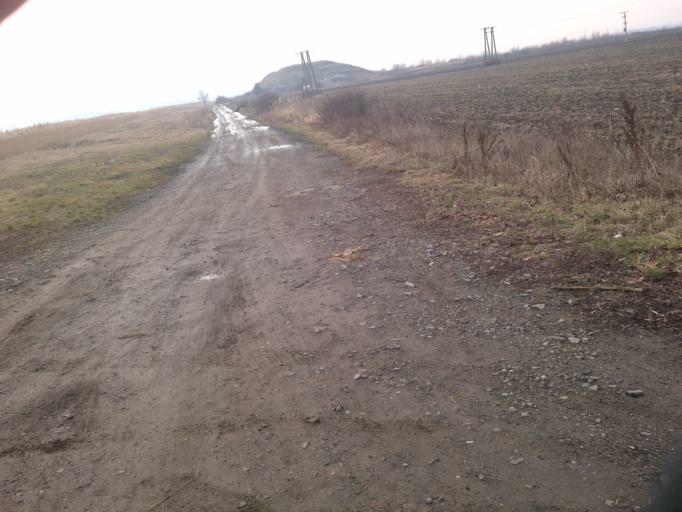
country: HU
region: Borsod-Abauj-Zemplen
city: Encs
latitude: 48.3254
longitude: 21.1465
